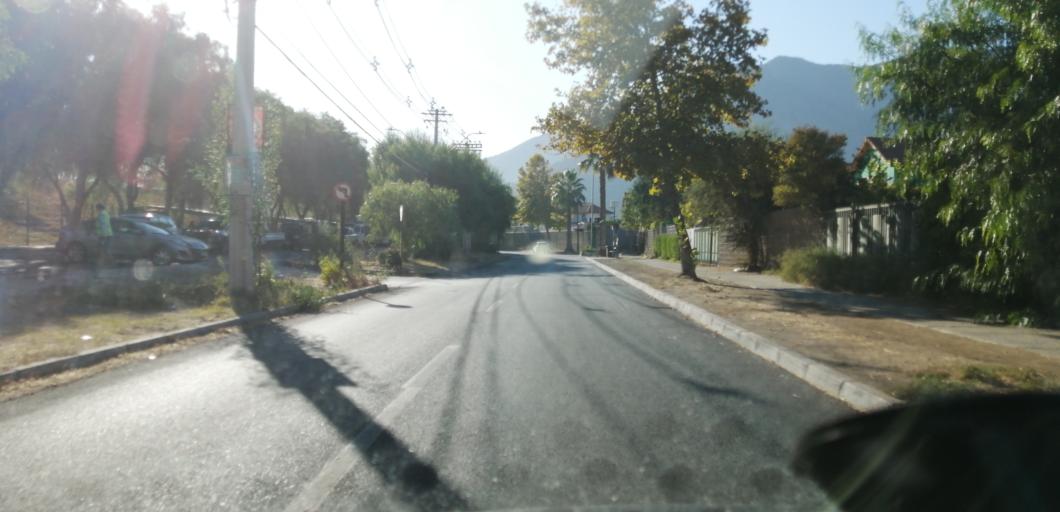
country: CL
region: Santiago Metropolitan
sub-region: Provincia de Santiago
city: Lo Prado
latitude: -33.4529
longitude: -70.8525
